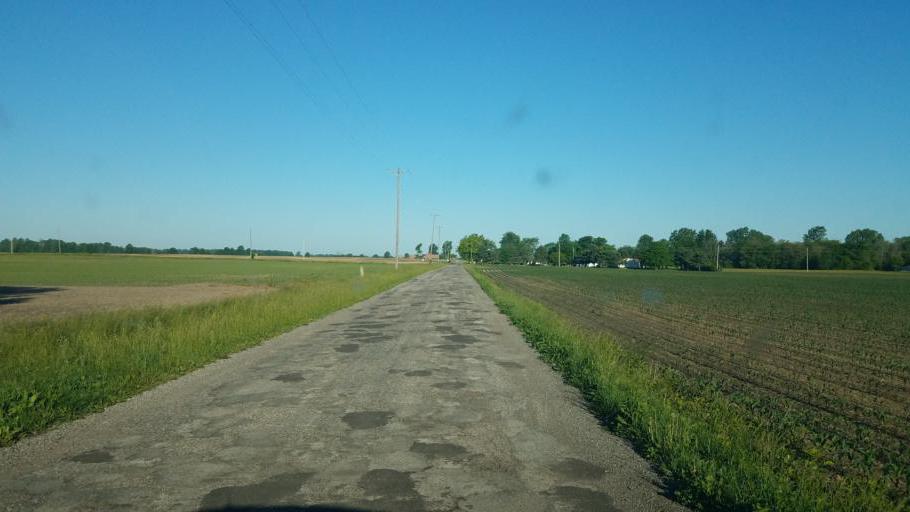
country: US
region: Ohio
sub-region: Morrow County
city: Mount Gilead
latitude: 40.6160
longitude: -82.8966
